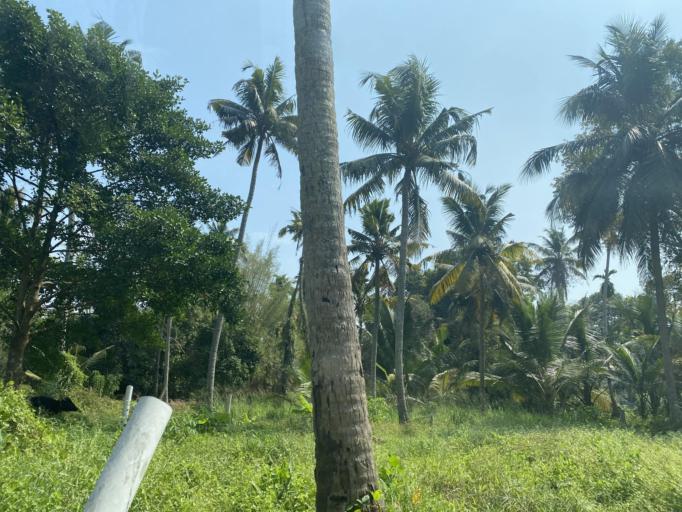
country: IN
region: Kerala
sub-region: Ernakulam
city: Elur
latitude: 10.1080
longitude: 76.2312
